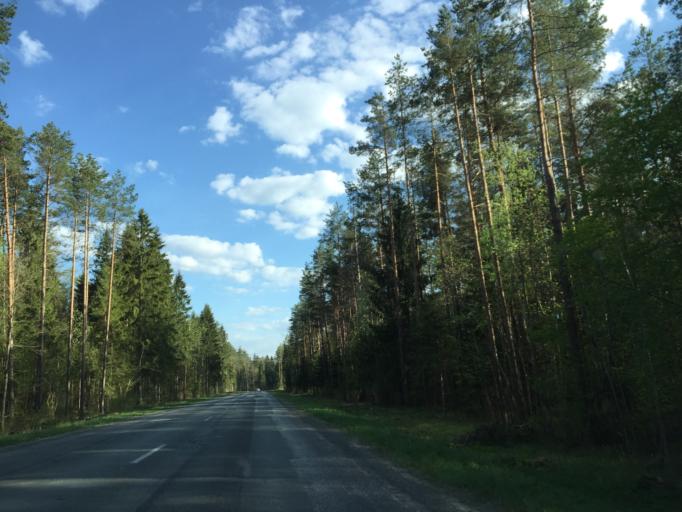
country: LV
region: Sigulda
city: Sigulda
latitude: 57.2250
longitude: 24.8533
